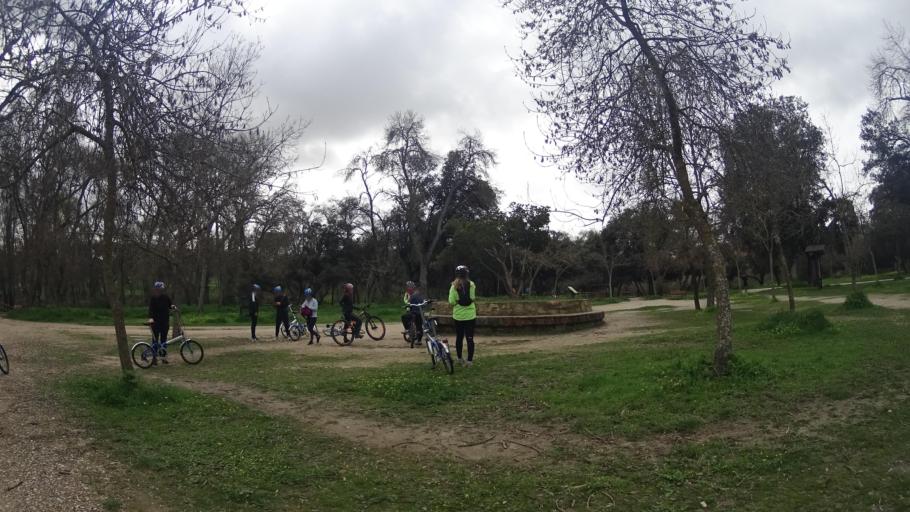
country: ES
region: Madrid
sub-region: Provincia de Madrid
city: Latina
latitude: 40.4021
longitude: -3.7725
